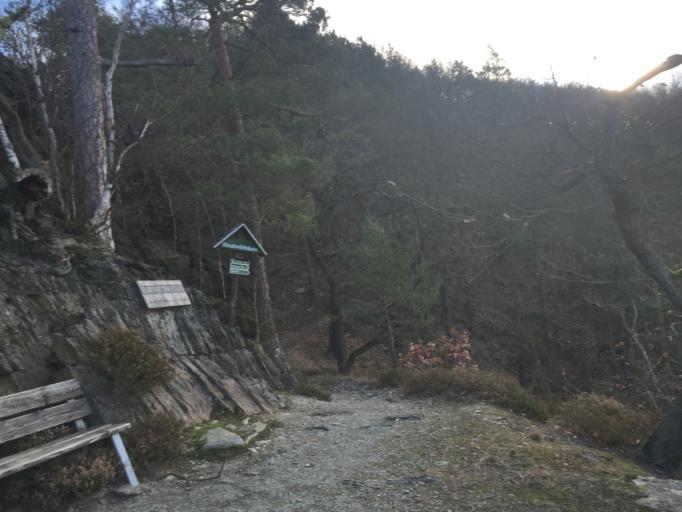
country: DE
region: Thuringia
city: Bad Blankenburg
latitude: 50.6654
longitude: 11.2526
